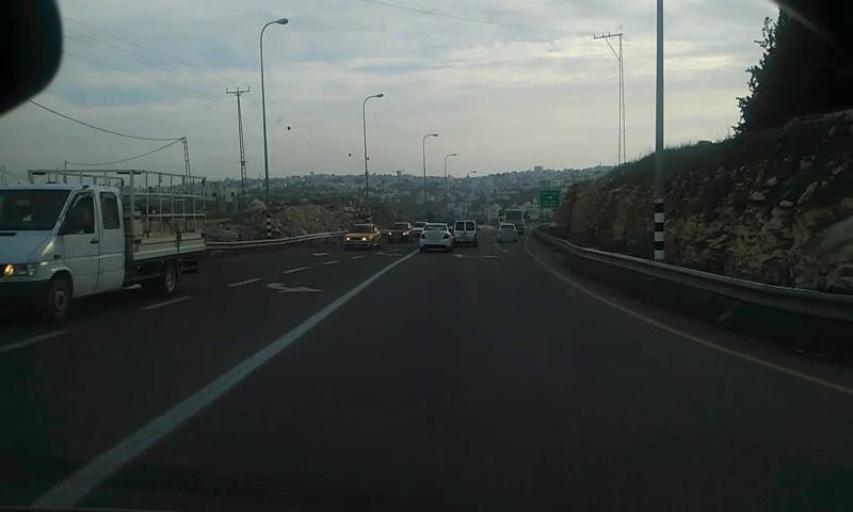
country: PS
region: West Bank
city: Halhul
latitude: 31.6007
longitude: 35.1103
